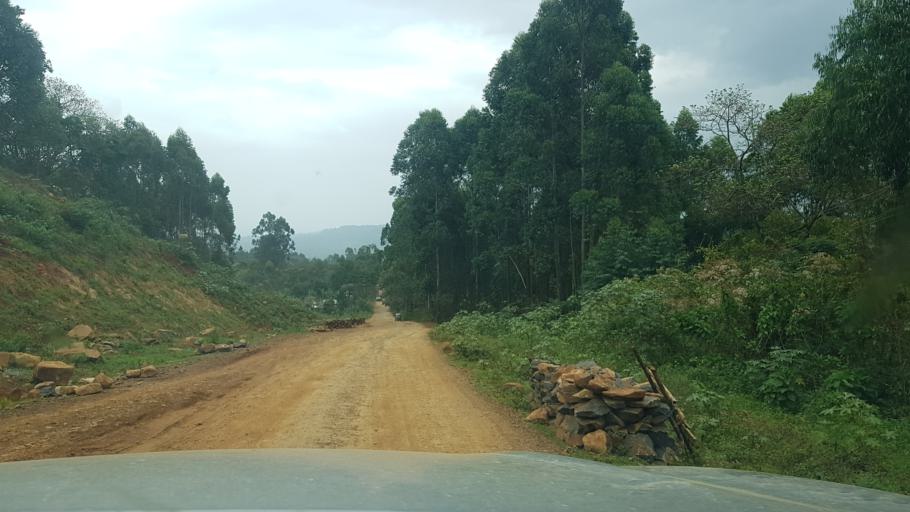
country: ET
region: Oromiya
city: Gore
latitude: 7.8288
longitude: 35.4657
